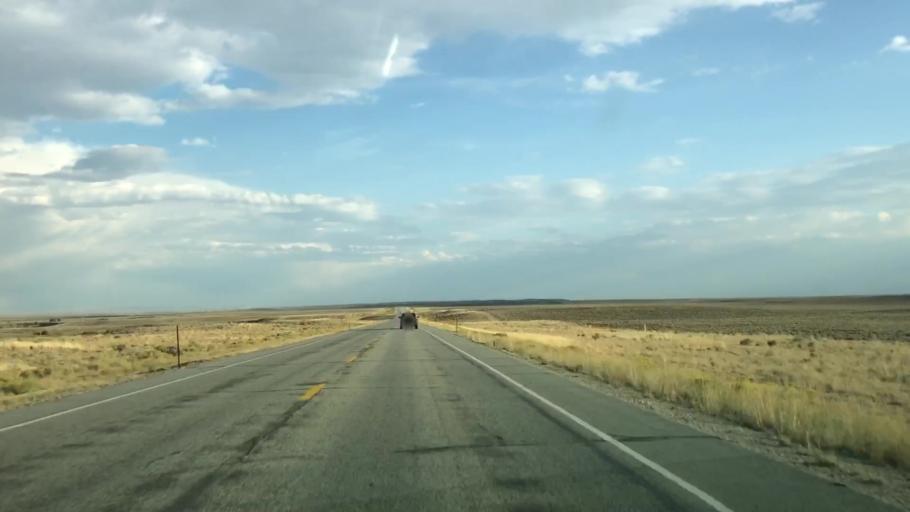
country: US
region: Wyoming
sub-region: Sublette County
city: Marbleton
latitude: 42.3320
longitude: -109.5168
